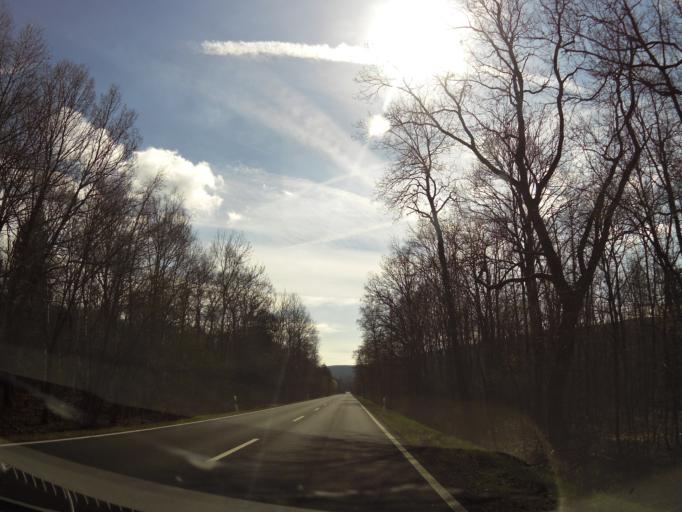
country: DE
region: Thuringia
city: Luisenthal
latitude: 50.8040
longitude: 10.7463
